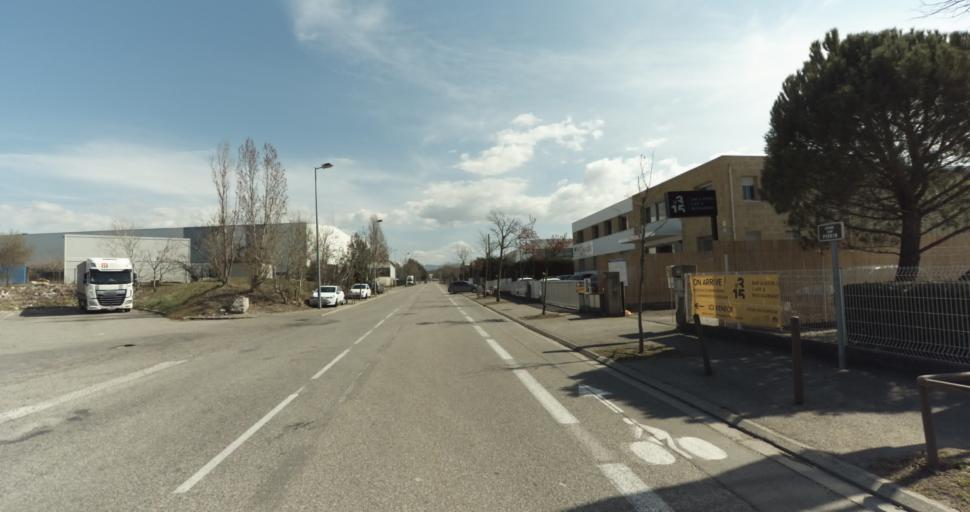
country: FR
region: Provence-Alpes-Cote d'Azur
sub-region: Departement des Bouches-du-Rhone
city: Cabries
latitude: 43.4832
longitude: 5.3765
